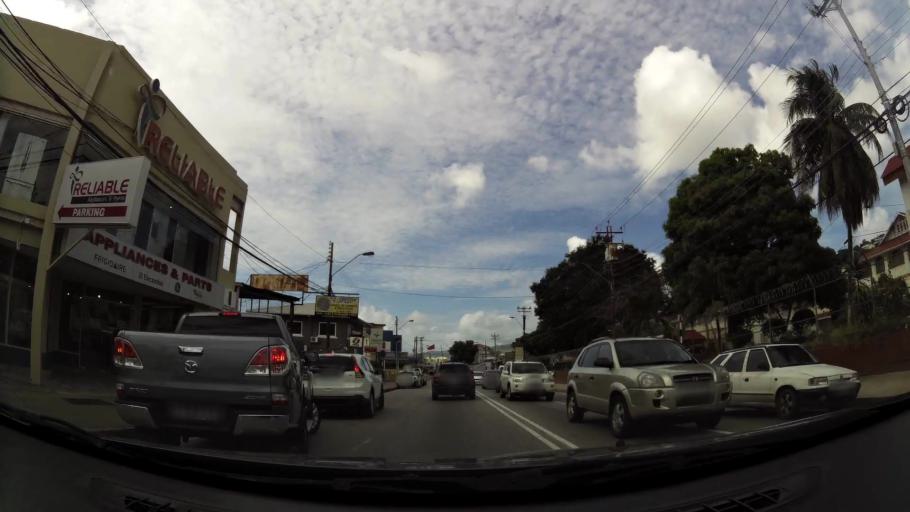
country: TT
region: City of Port of Spain
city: Mucurapo
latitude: 10.6735
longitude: -61.5391
